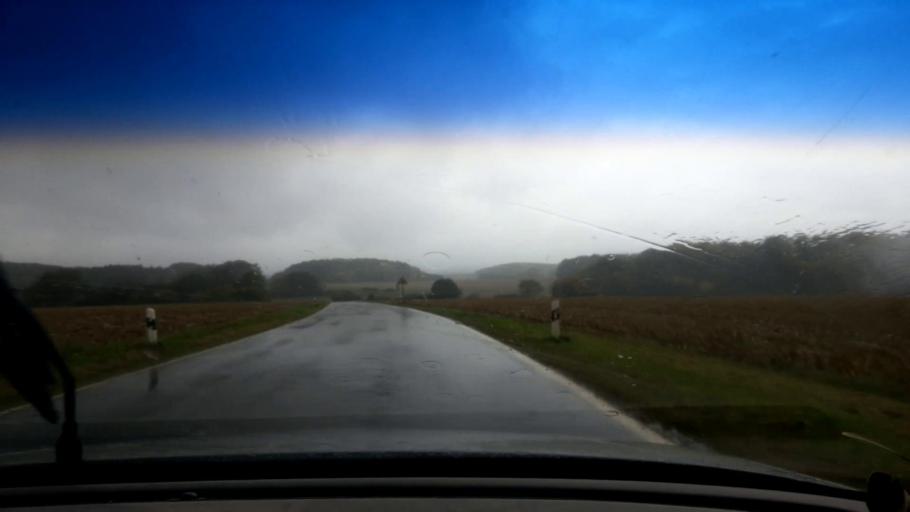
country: DE
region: Bavaria
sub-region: Upper Franconia
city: Stadelhofen
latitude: 50.0434
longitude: 11.1962
